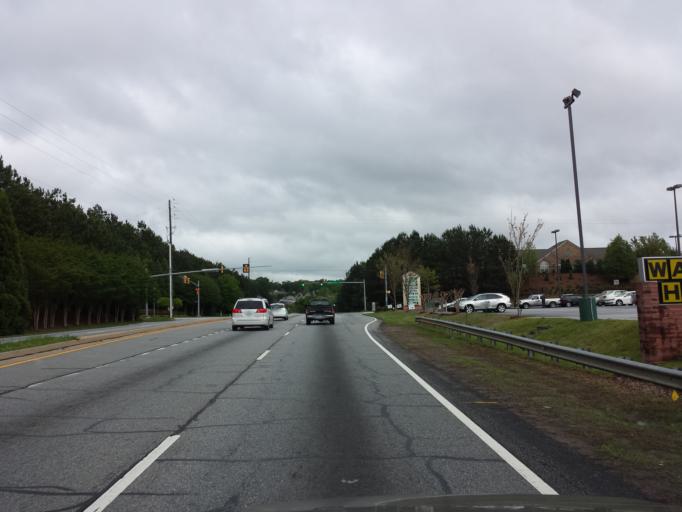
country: US
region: Georgia
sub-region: Cobb County
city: Smyrna
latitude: 33.8409
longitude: -84.5191
